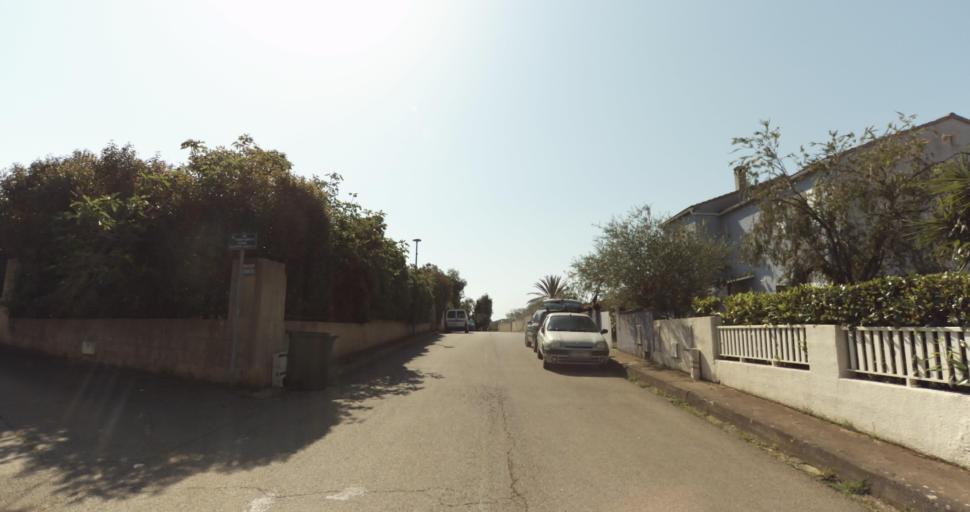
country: FR
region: Corsica
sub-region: Departement de la Haute-Corse
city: Biguglia
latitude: 42.6231
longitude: 9.4292
